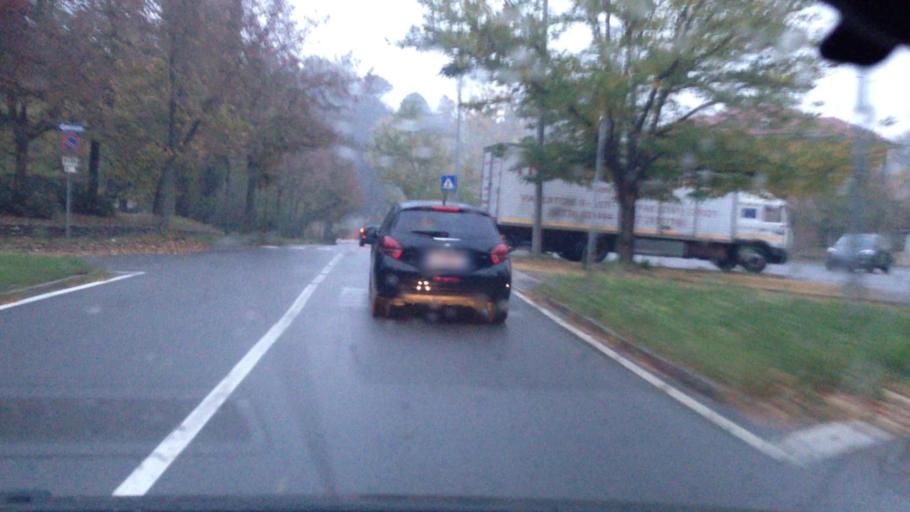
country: IT
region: Piedmont
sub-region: Provincia di Asti
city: Asti
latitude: 44.9133
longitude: 8.2109
